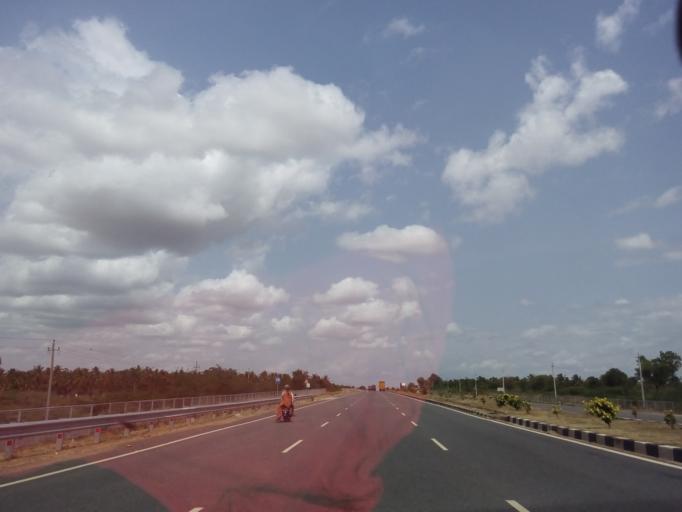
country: IN
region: Karnataka
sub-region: Tumkur
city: Sira
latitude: 13.8201
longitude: 76.7785
